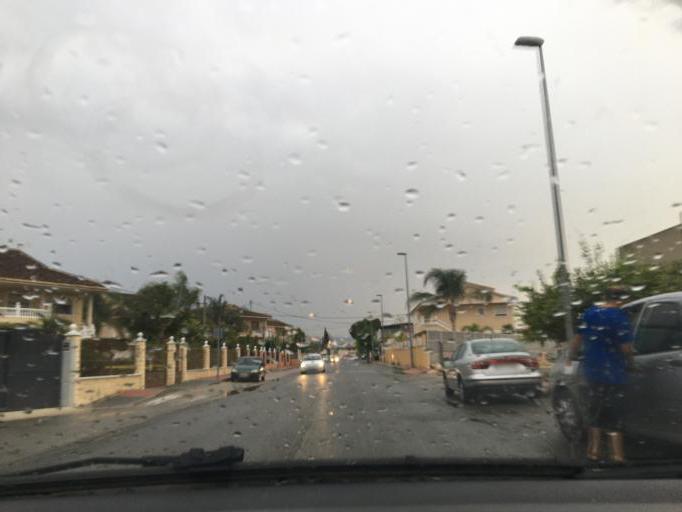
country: ES
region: Murcia
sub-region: Murcia
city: Santomera
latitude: 38.0293
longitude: -1.0454
